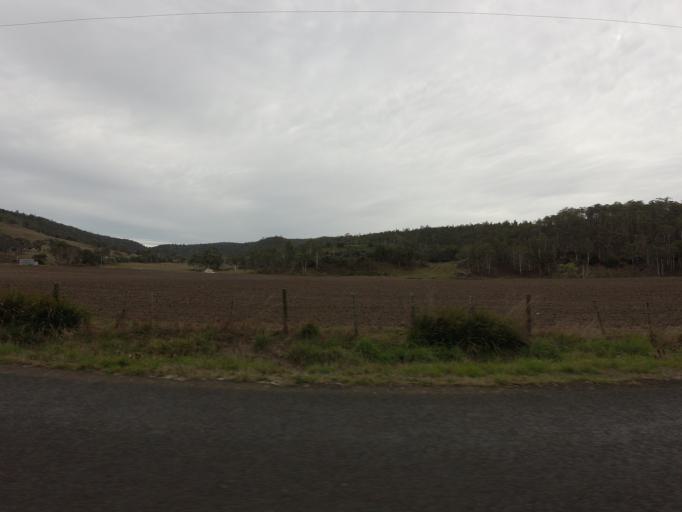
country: AU
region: Tasmania
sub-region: Derwent Valley
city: New Norfolk
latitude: -42.5988
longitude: 147.0541
